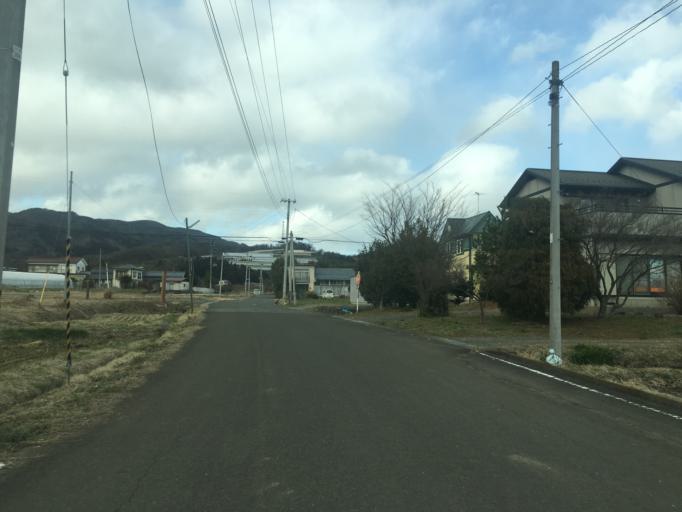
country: JP
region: Fukushima
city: Yanagawamachi-saiwaicho
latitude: 37.8884
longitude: 140.5821
